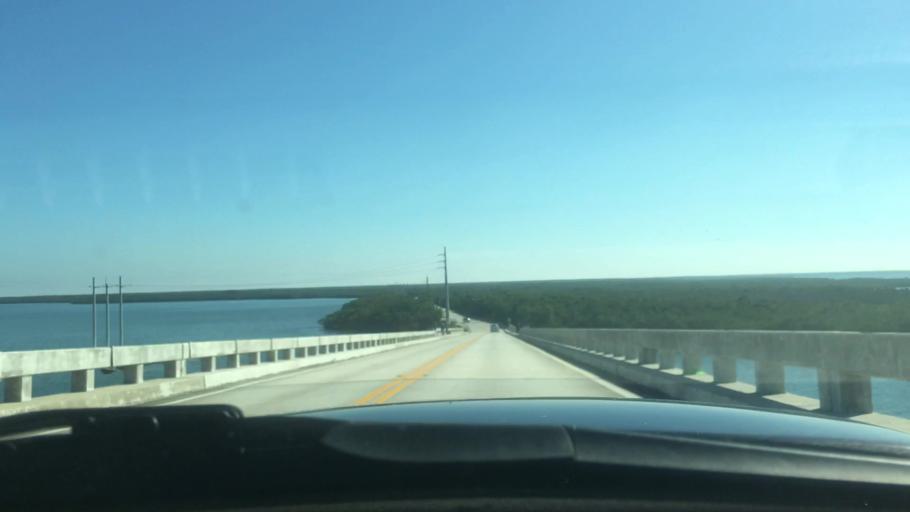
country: US
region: Florida
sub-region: Monroe County
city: North Key Largo
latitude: 25.2865
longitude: -80.3666
